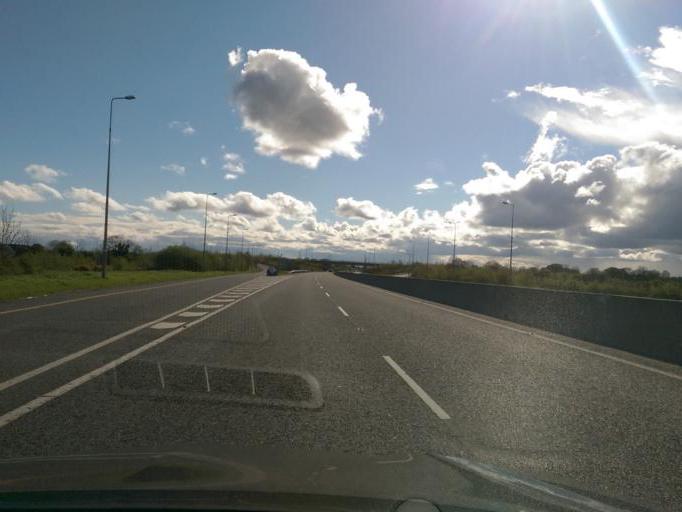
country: IE
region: Leinster
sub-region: An Iarmhi
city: Rochfortbridge
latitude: 53.4077
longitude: -7.2779
